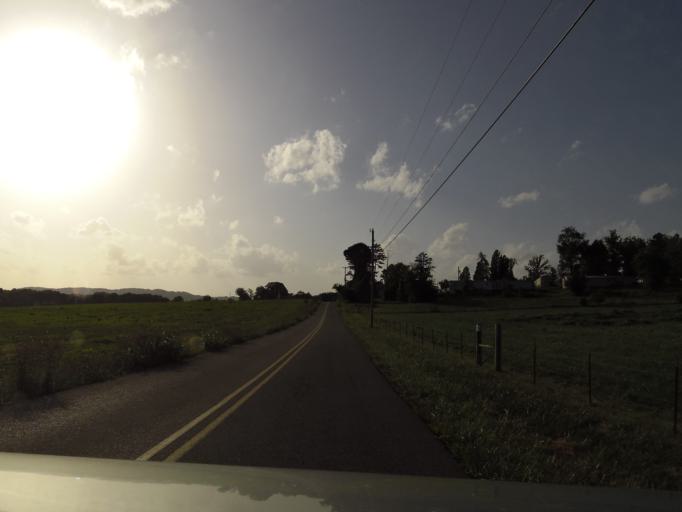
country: US
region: Tennessee
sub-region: Blount County
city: Wildwood
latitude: 35.8238
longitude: -83.8815
